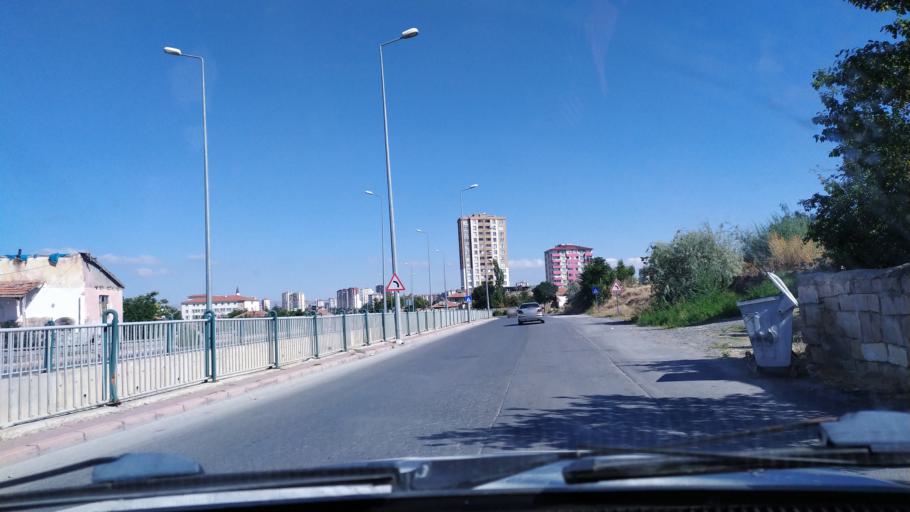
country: TR
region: Kayseri
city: Talas
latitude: 38.7261
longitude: 35.5506
